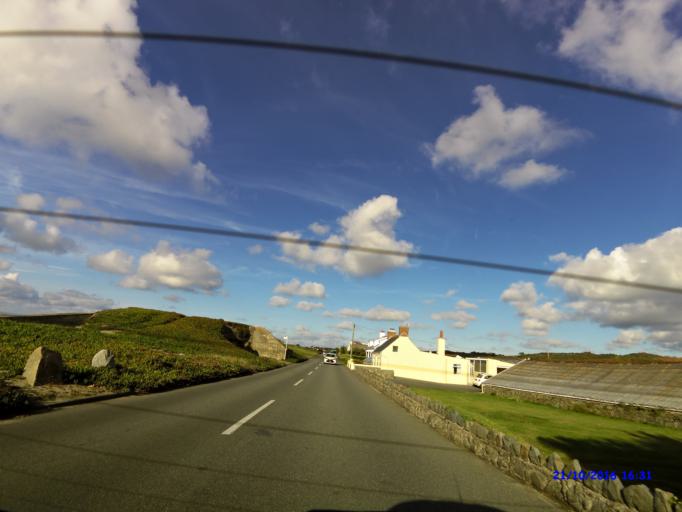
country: GG
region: St Peter Port
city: Saint Peter Port
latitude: 49.4423
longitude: -2.6500
